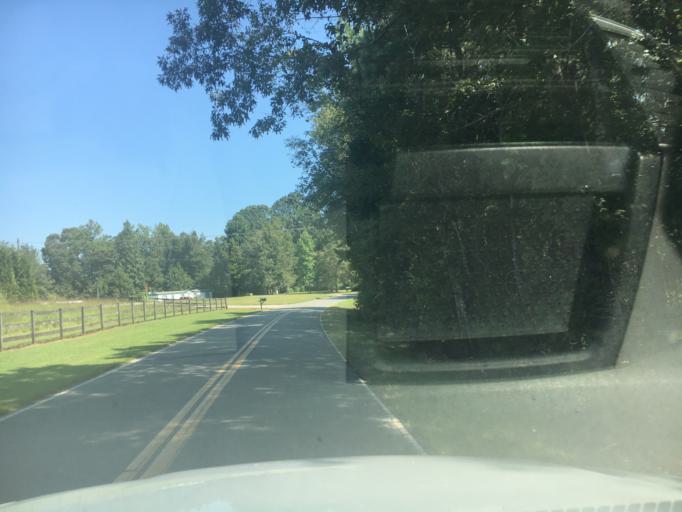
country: US
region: South Carolina
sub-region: Spartanburg County
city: Landrum
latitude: 35.1929
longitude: -82.0391
